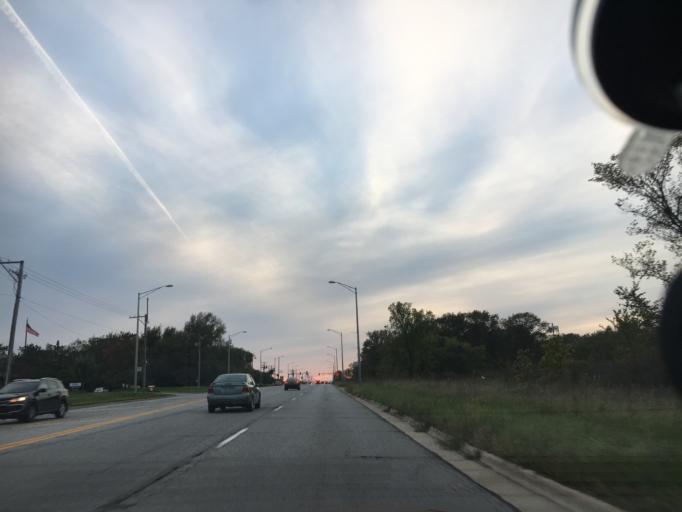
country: US
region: Illinois
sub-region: Cook County
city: Tinley Park
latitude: 41.6026
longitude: -87.7809
